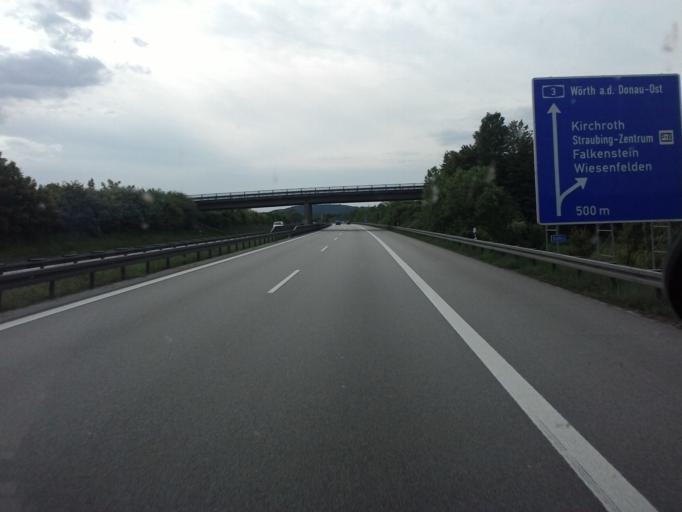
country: DE
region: Bavaria
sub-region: Lower Bavaria
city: Kirchroth
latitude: 48.9548
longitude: 12.5530
